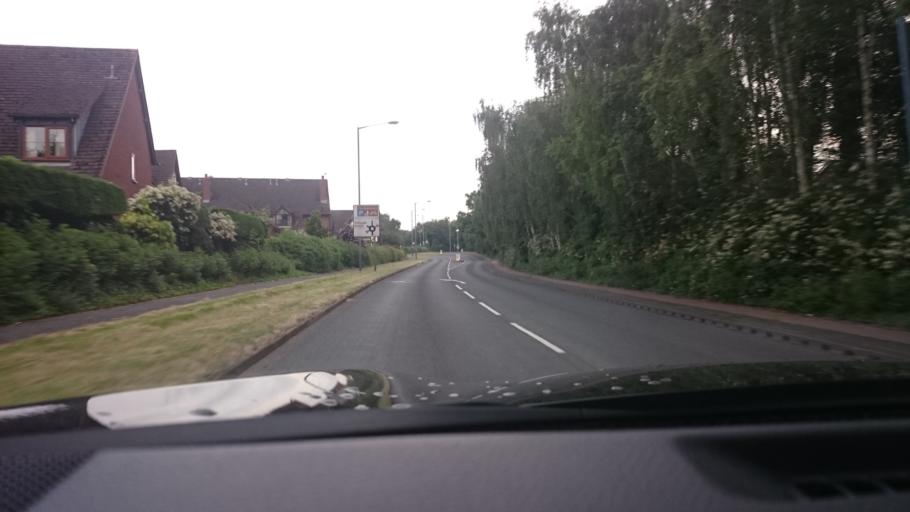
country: GB
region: England
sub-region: Warwickshire
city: Stratford-upon-Avon
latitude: 52.1866
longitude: -1.7137
